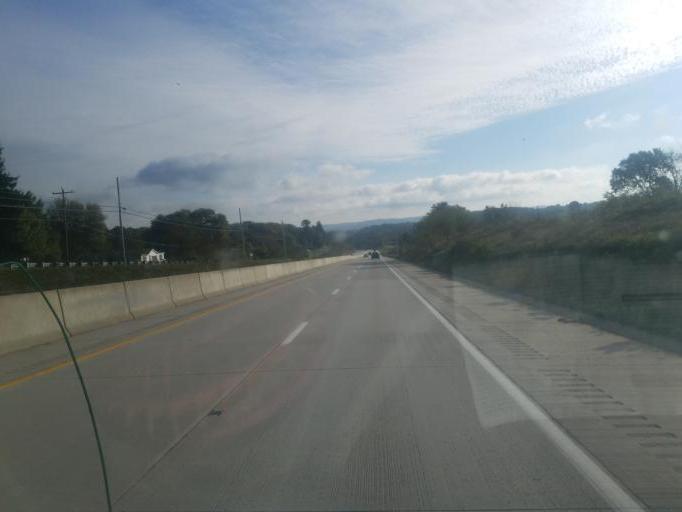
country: US
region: Pennsylvania
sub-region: Indiana County
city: Blairsville
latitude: 40.4279
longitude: -79.3037
